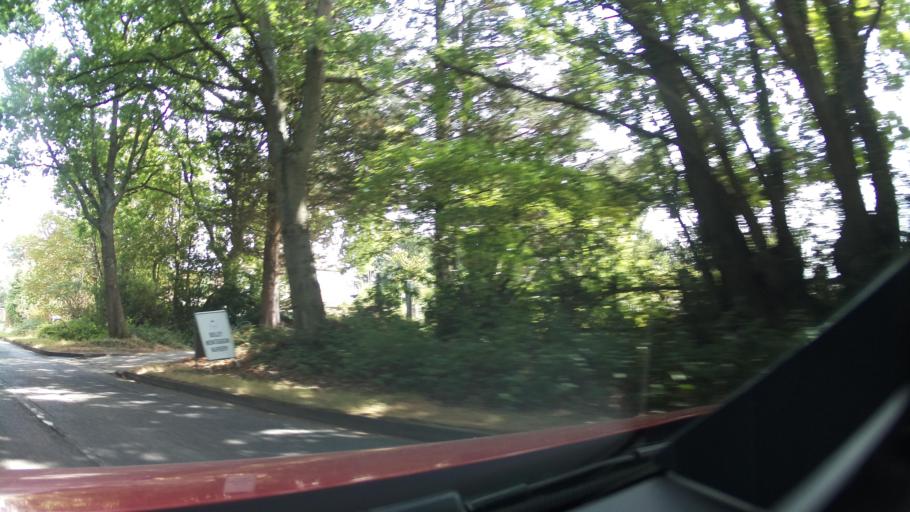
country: GB
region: England
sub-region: Surrey
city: Knaphill
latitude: 51.3201
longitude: -0.6371
